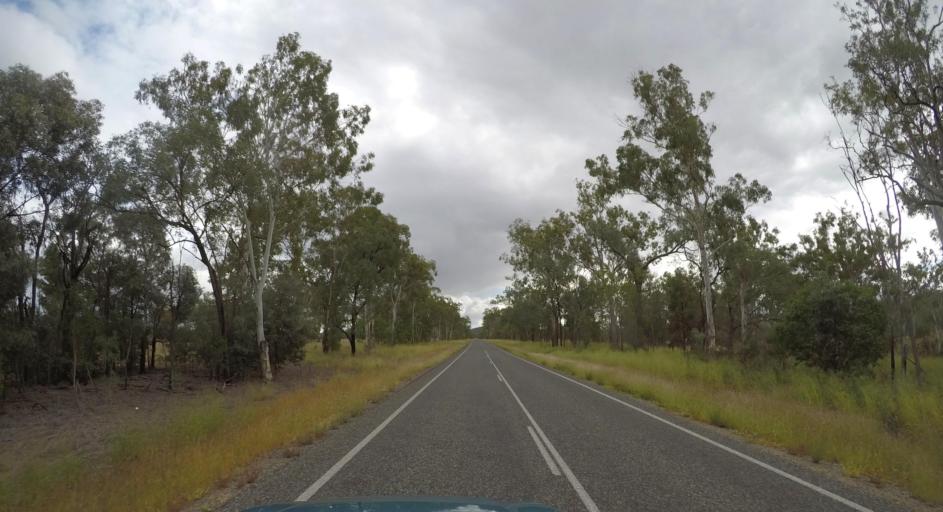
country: AU
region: Queensland
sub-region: North Burnett
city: Gayndah
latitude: -25.4987
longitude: 151.2697
